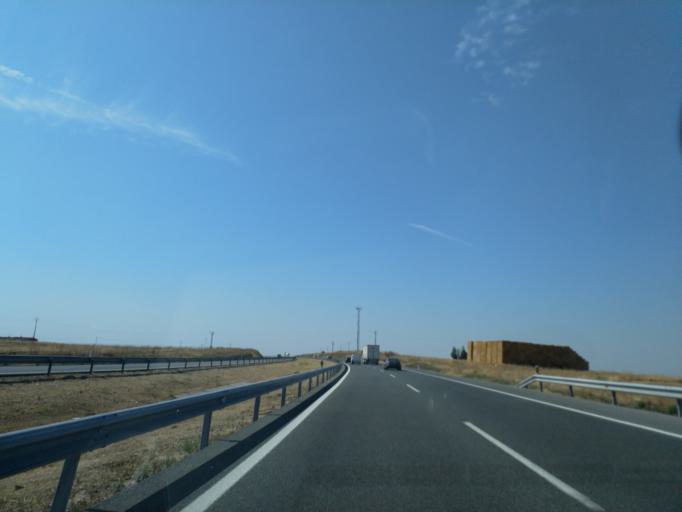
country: ES
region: Castille-La Mancha
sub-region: Province of Toledo
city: Quismondo
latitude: 40.1101
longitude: -4.3304
